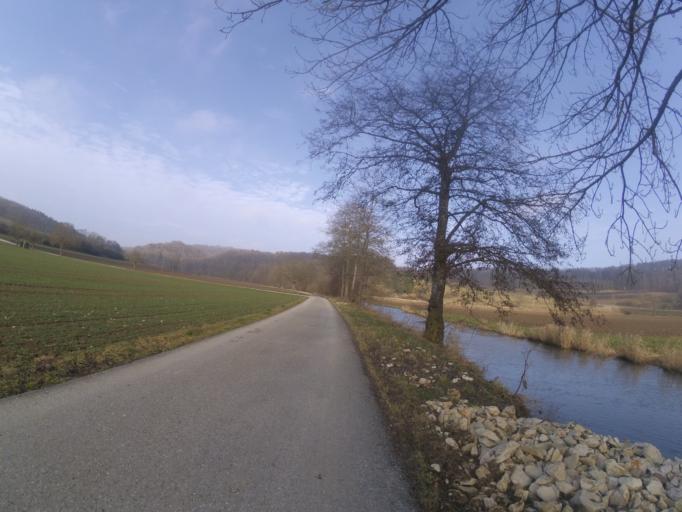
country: DE
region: Baden-Wuerttemberg
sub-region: Tuebingen Region
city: Rechtenstein
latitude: 48.2672
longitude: 9.5419
